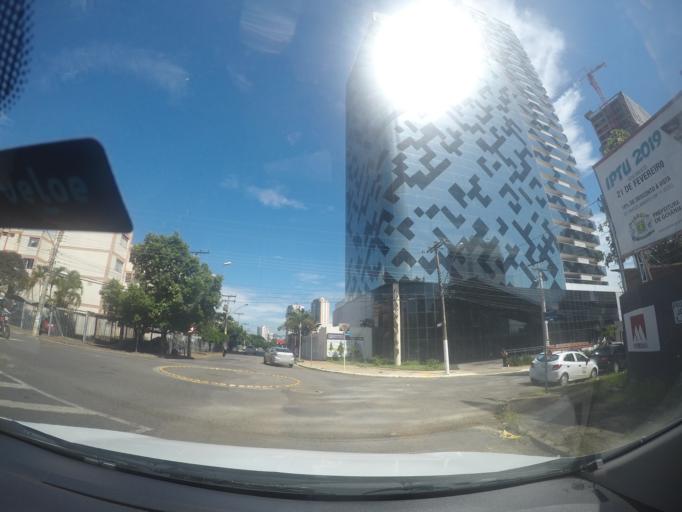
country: BR
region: Goias
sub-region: Goiania
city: Goiania
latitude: -16.6952
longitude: -49.2622
